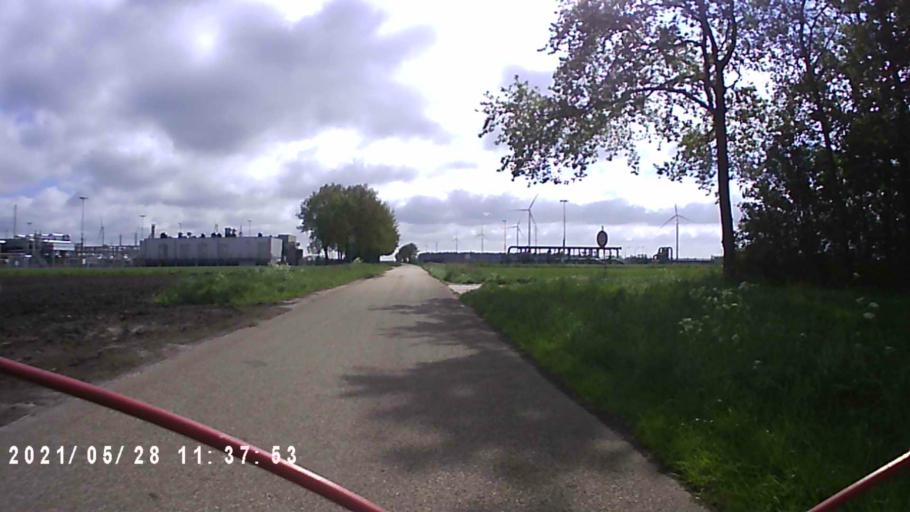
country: NL
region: Groningen
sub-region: Gemeente Veendam
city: Veendam
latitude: 53.1522
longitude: 6.8700
